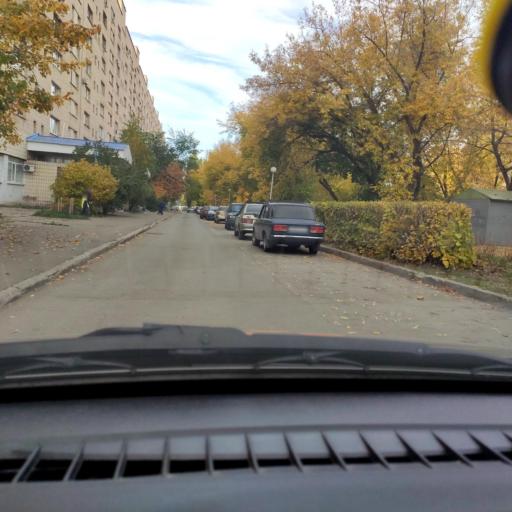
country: RU
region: Samara
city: Tol'yatti
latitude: 53.5219
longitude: 49.2662
